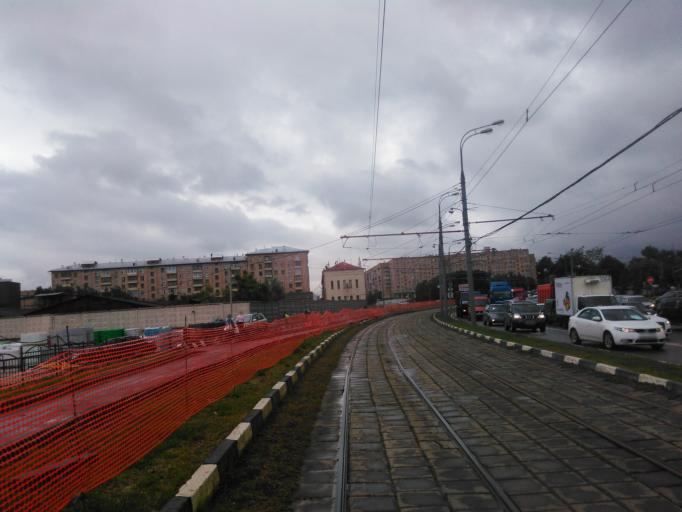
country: RU
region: Moscow
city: Nagornyy
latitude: 55.6735
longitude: 37.6275
